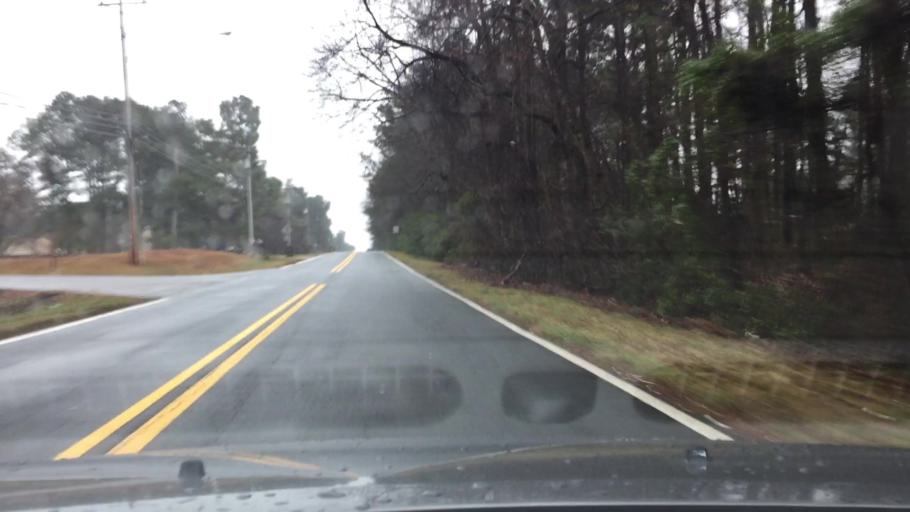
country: US
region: Georgia
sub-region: Cobb County
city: Fair Oaks
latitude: 33.9138
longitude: -84.6099
